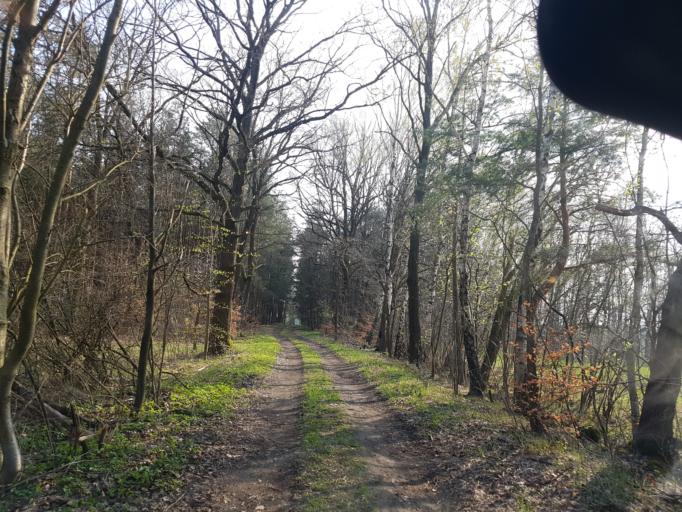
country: DE
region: Brandenburg
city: Schonborn
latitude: 51.6050
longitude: 13.5148
